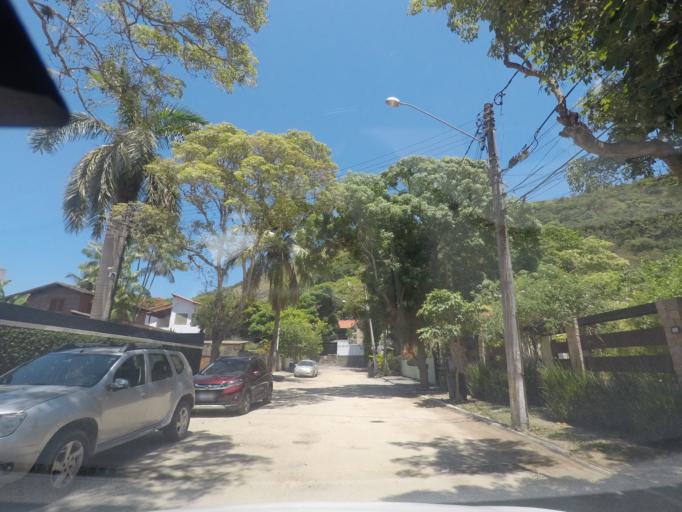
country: BR
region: Rio de Janeiro
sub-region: Niteroi
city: Niteroi
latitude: -22.9705
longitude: -43.0335
